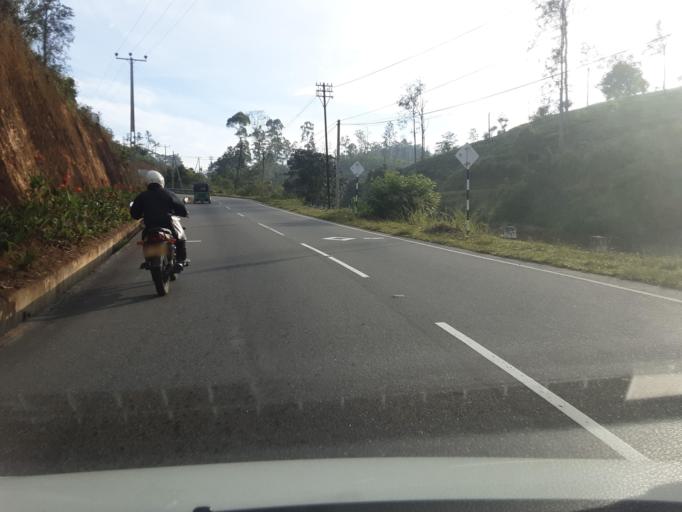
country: LK
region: Uva
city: Badulla
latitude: 6.9309
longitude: 80.9820
